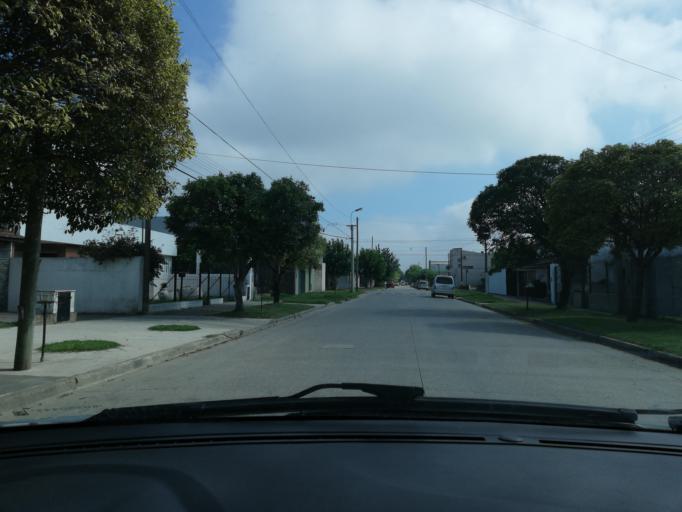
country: AR
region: Buenos Aires
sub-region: Partido de Balcarce
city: Balcarce
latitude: -37.8460
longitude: -58.2463
